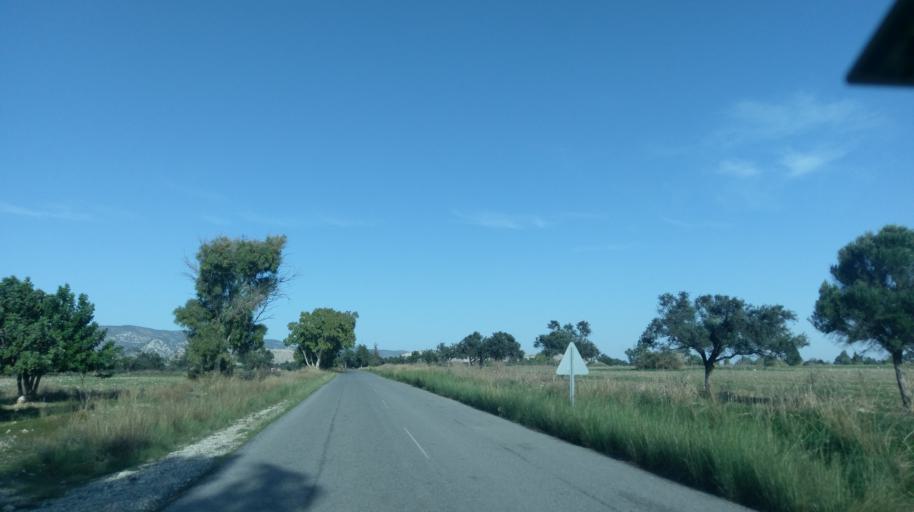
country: CY
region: Ammochostos
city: Lefkonoiko
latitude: 35.2956
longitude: 33.7391
